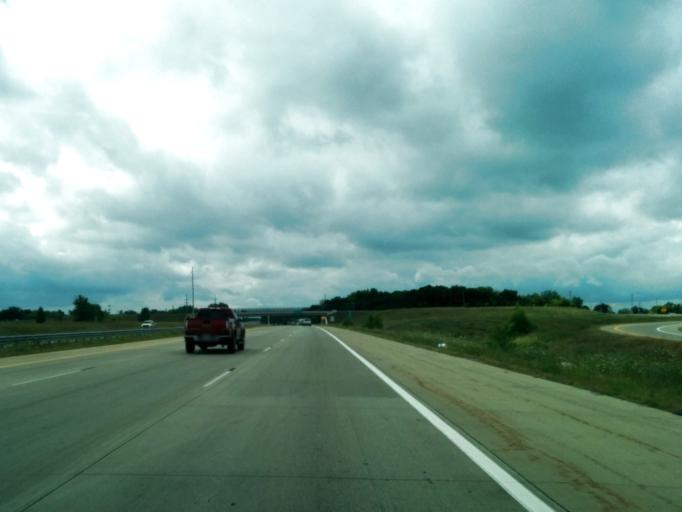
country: US
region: Michigan
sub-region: Oakland County
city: Rochester Hills
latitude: 42.6448
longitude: -83.1658
